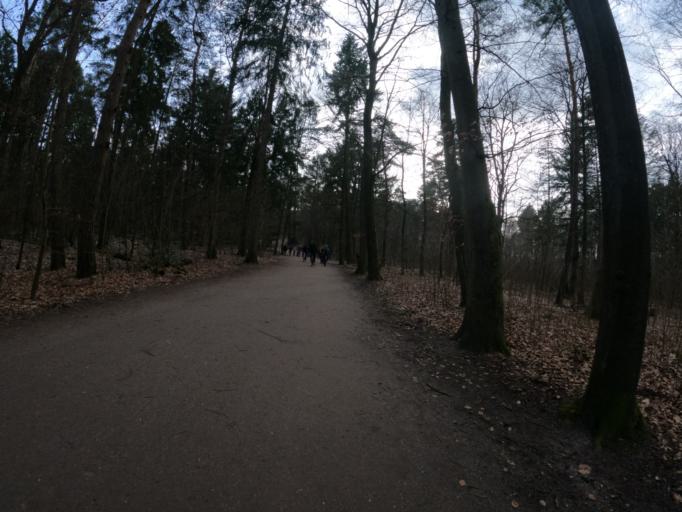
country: DE
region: Hamburg
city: Eidelstedt
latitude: 53.5824
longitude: 9.8924
